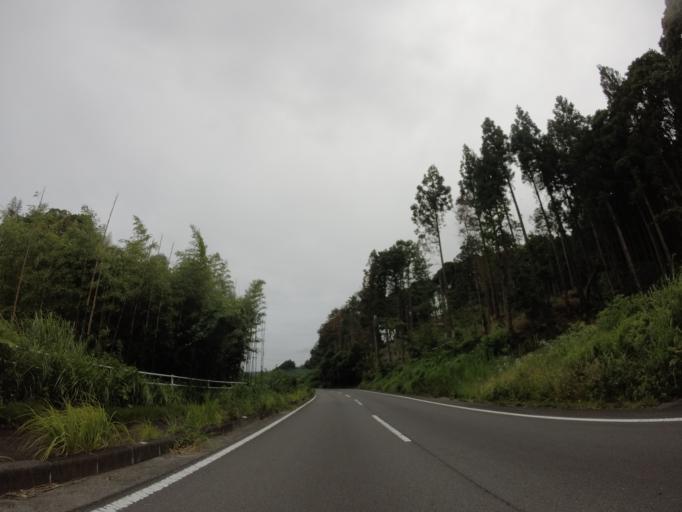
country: JP
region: Shizuoka
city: Kanaya
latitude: 34.7938
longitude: 138.1443
